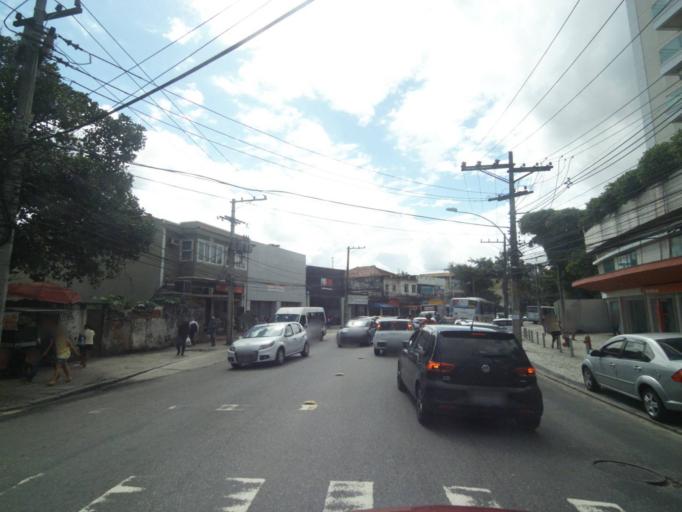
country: BR
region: Rio de Janeiro
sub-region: Sao Joao De Meriti
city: Sao Joao de Meriti
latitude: -22.9240
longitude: -43.3614
